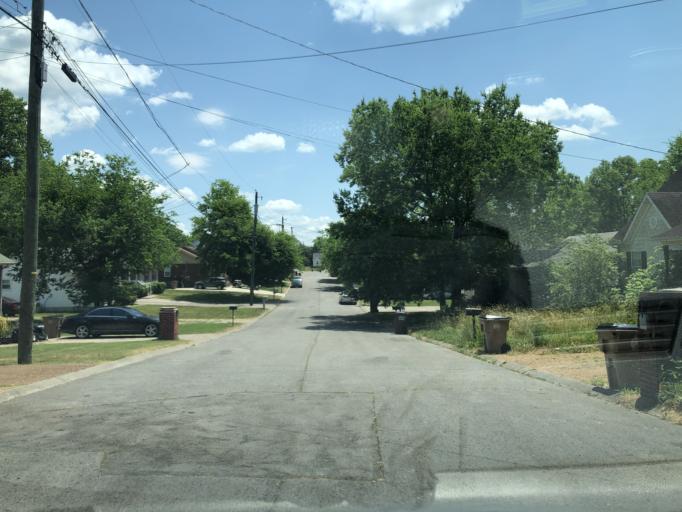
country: US
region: Tennessee
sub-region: Davidson County
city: Goodlettsville
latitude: 36.2704
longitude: -86.7188
